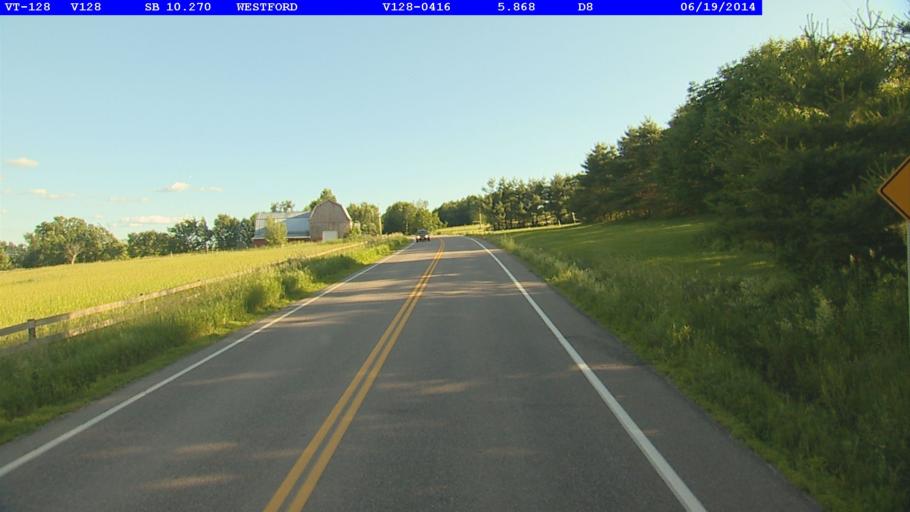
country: US
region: Vermont
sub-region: Chittenden County
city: Milton
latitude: 44.6376
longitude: -73.0170
